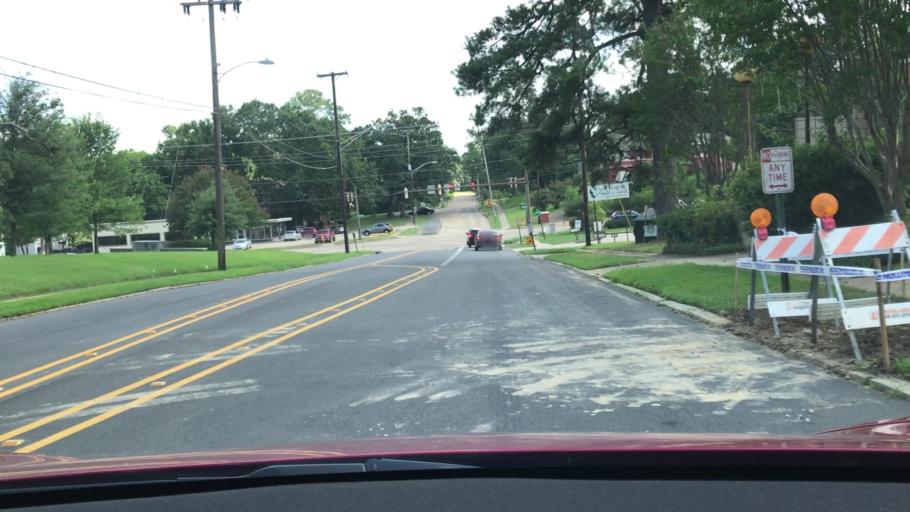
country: US
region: Louisiana
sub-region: Bossier Parish
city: Bossier City
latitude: 32.4827
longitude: -93.7339
